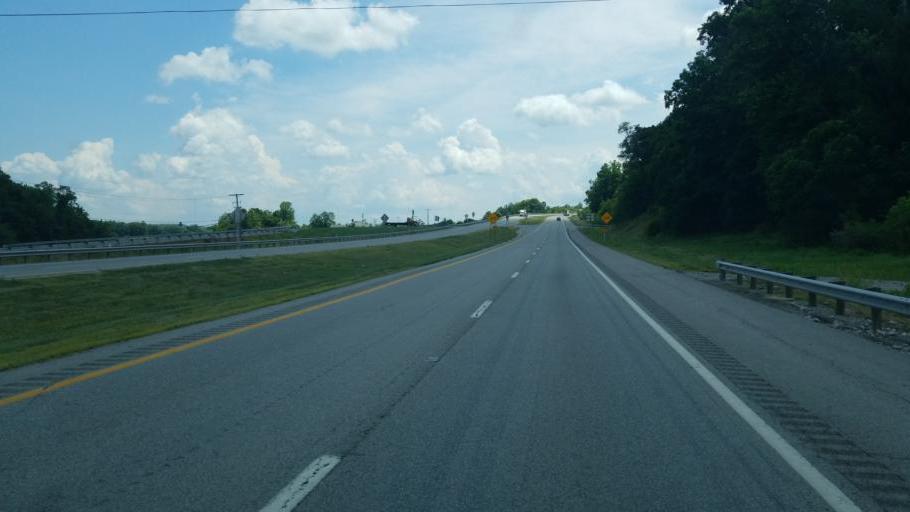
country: US
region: West Virginia
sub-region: Mason County
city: Point Pleasant
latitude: 38.8142
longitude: -82.1115
